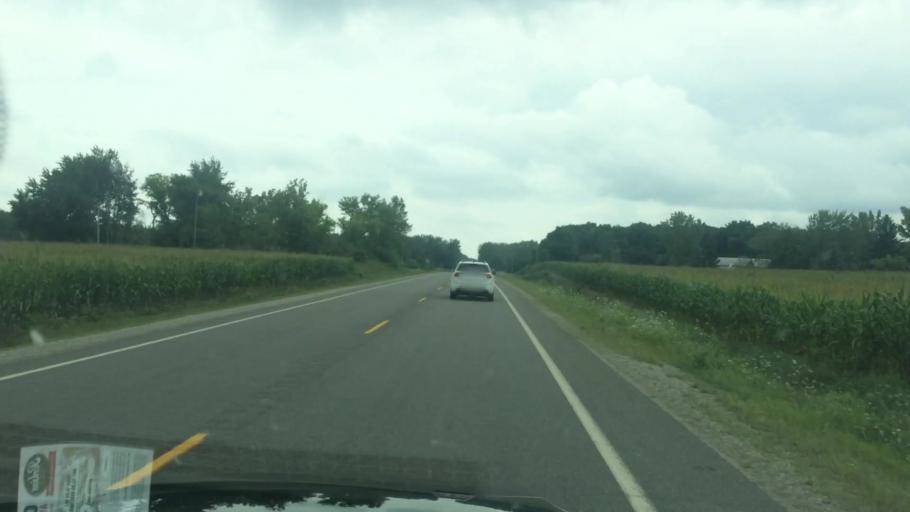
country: US
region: Michigan
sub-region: Tuscola County
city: Cass City
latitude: 43.6328
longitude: -83.0972
